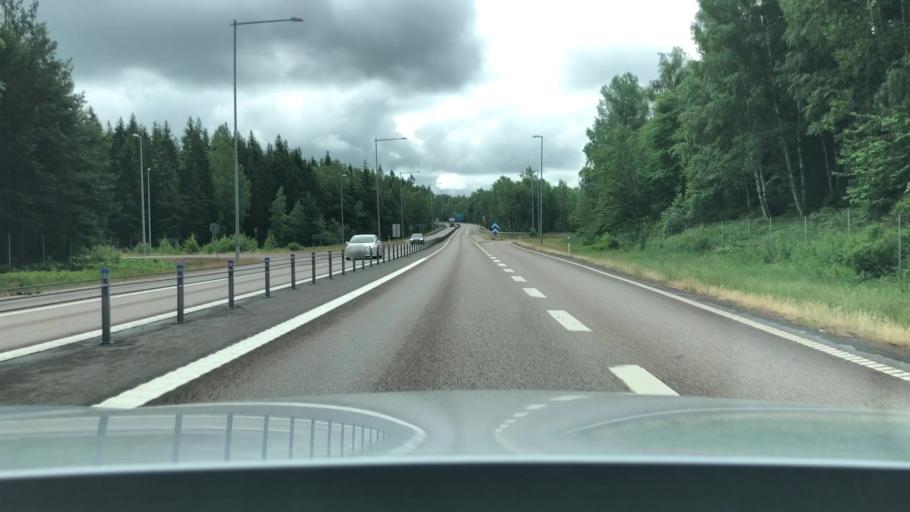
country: SE
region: Vaermland
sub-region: Kristinehamns Kommun
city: Kristinehamn
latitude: 59.3325
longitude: 14.0965
